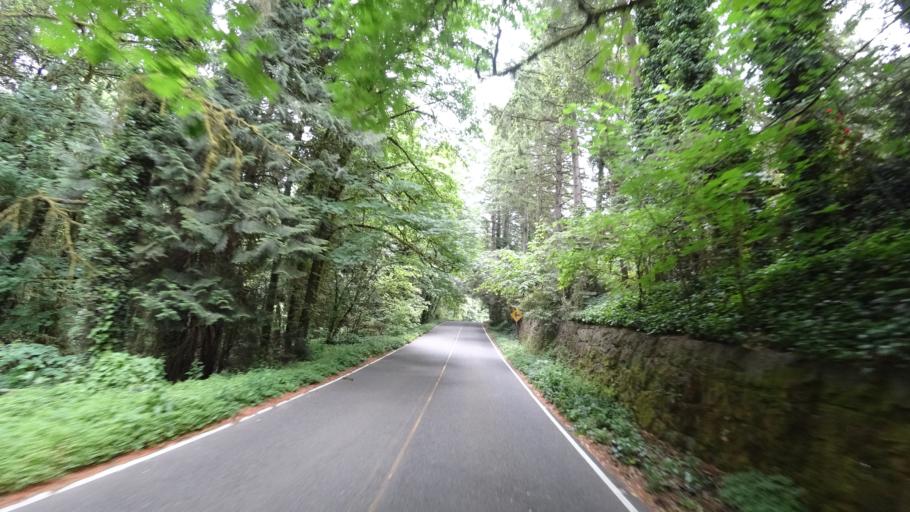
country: US
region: Oregon
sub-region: Clackamas County
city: Lake Oswego
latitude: 45.4572
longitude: -122.6965
